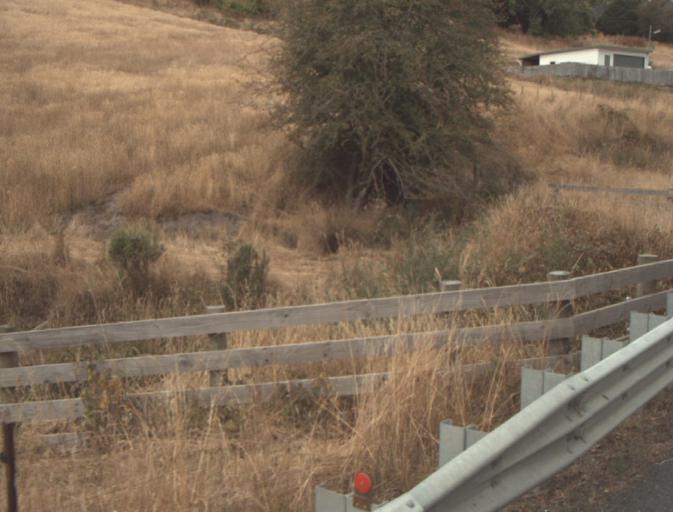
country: AU
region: Tasmania
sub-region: Launceston
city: Mayfield
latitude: -41.2355
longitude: 147.2137
